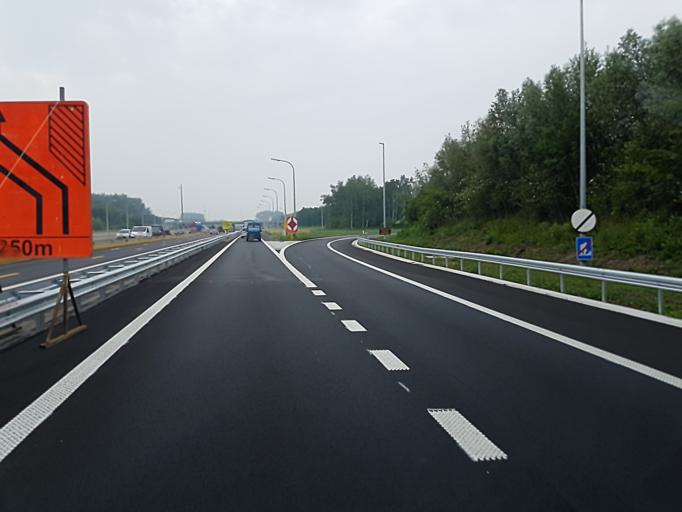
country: BE
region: Flanders
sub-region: Provincie West-Vlaanderen
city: Wevelgem
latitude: 50.8260
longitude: 3.1922
